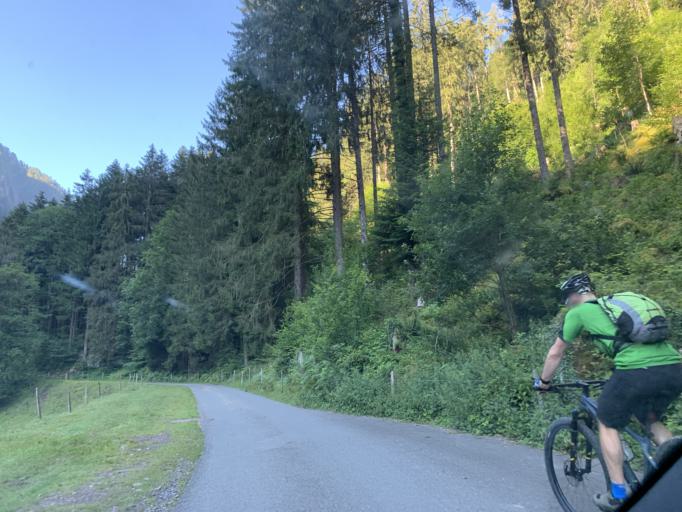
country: CH
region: Saint Gallen
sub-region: Wahlkreis Sarganserland
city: Quarten
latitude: 47.0969
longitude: 9.2099
